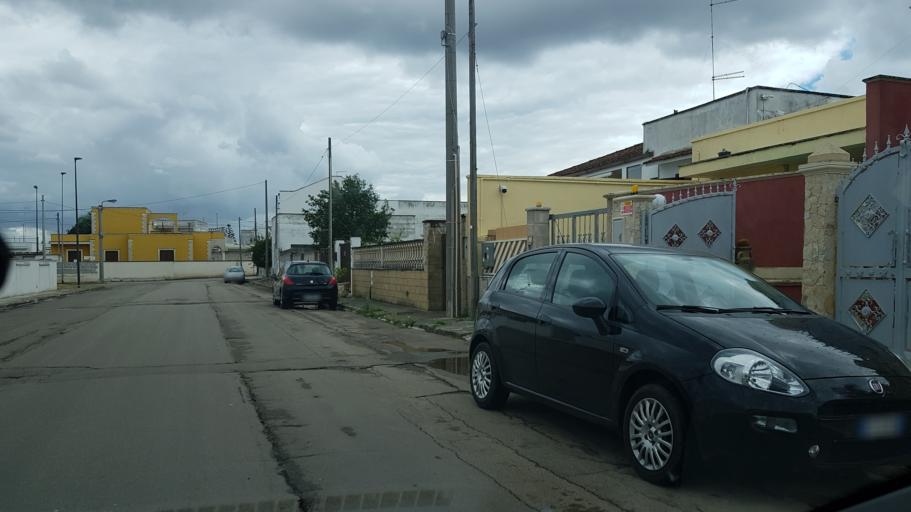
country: IT
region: Apulia
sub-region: Provincia di Brindisi
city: Torchiarolo
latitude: 40.4871
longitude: 18.0546
